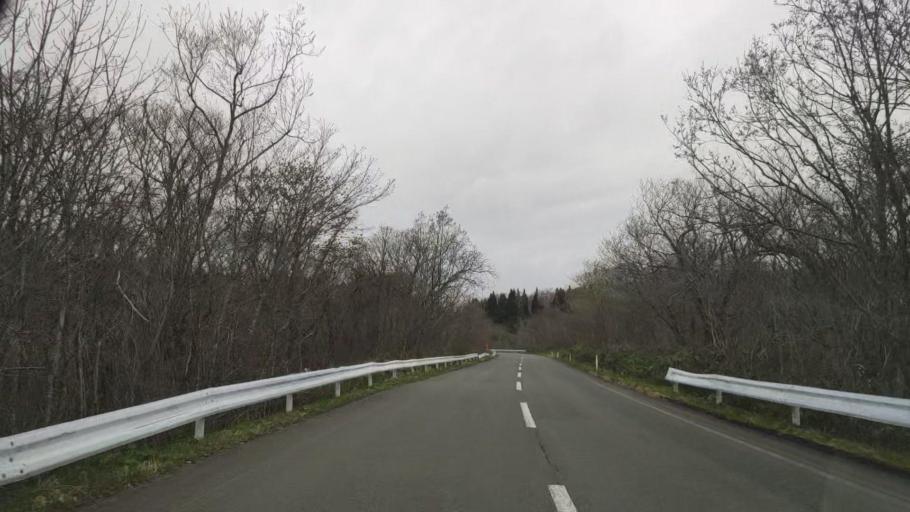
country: JP
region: Akita
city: Hanawa
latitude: 40.4093
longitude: 140.8490
